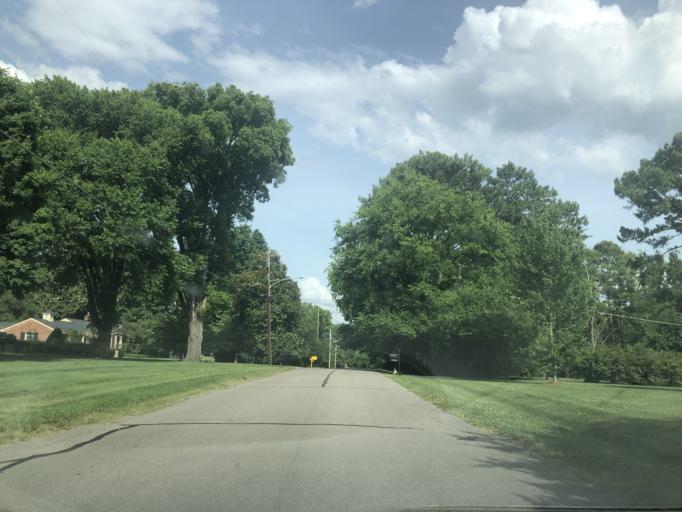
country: US
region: Tennessee
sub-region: Davidson County
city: Oak Hill
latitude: 36.0846
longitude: -86.7822
